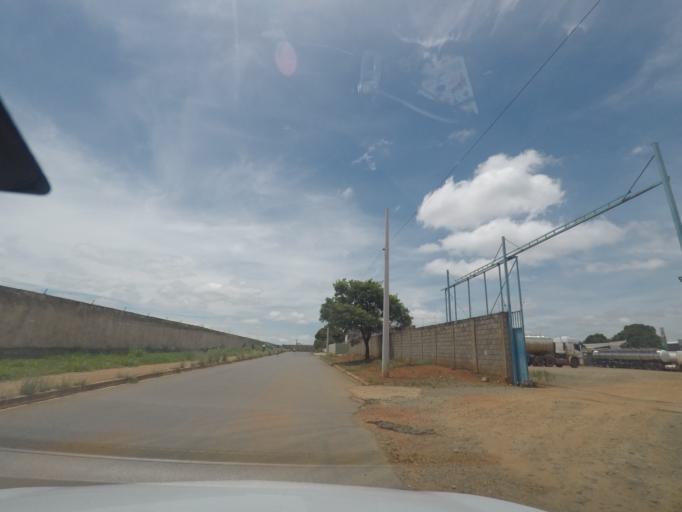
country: BR
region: Goias
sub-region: Goiania
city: Goiania
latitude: -16.6292
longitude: -49.2319
